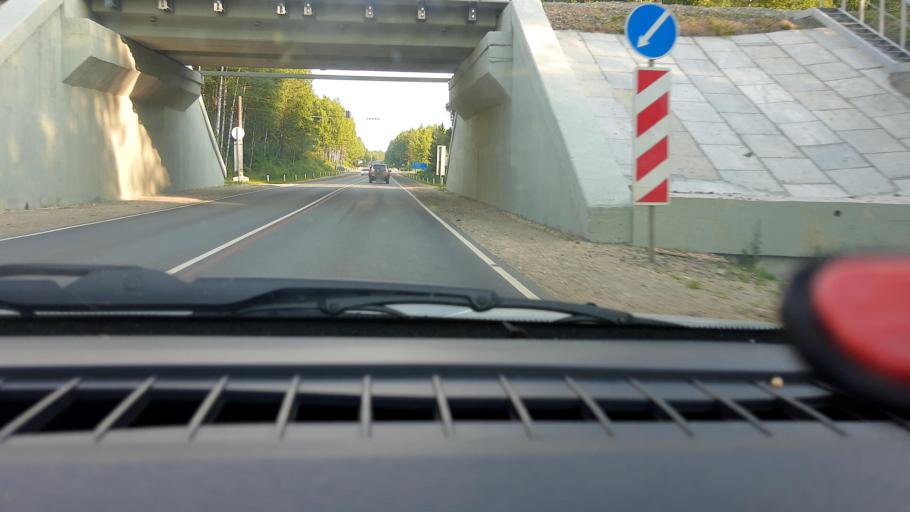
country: RU
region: Nizjnij Novgorod
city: Arzamas
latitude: 55.4318
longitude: 43.9005
